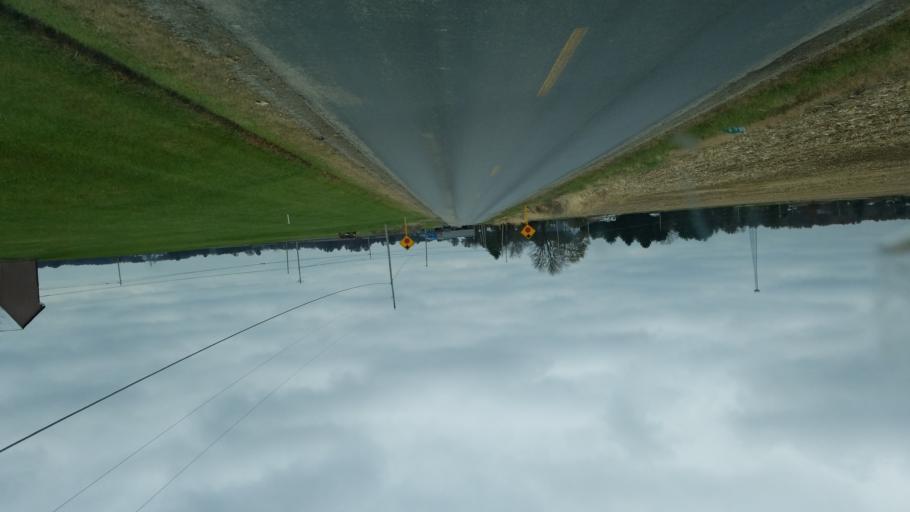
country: US
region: Ohio
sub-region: Licking County
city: Johnstown
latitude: 40.1912
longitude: -82.7571
